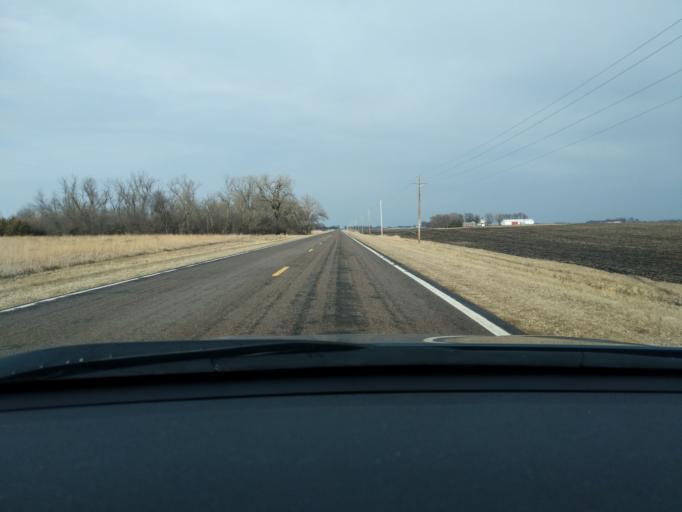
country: US
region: Minnesota
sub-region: Renville County
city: Renville
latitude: 44.7533
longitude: -95.3408
